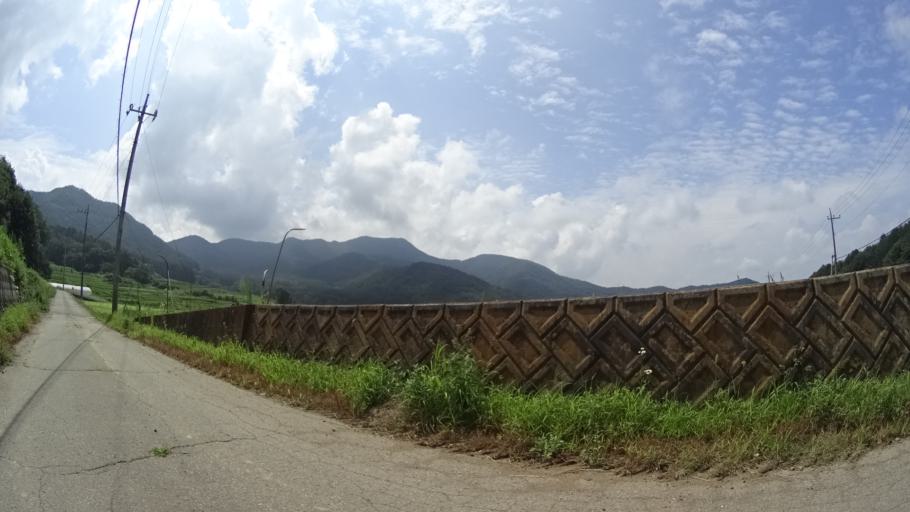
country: JP
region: Yamanashi
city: Nirasaki
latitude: 35.8934
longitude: 138.4702
